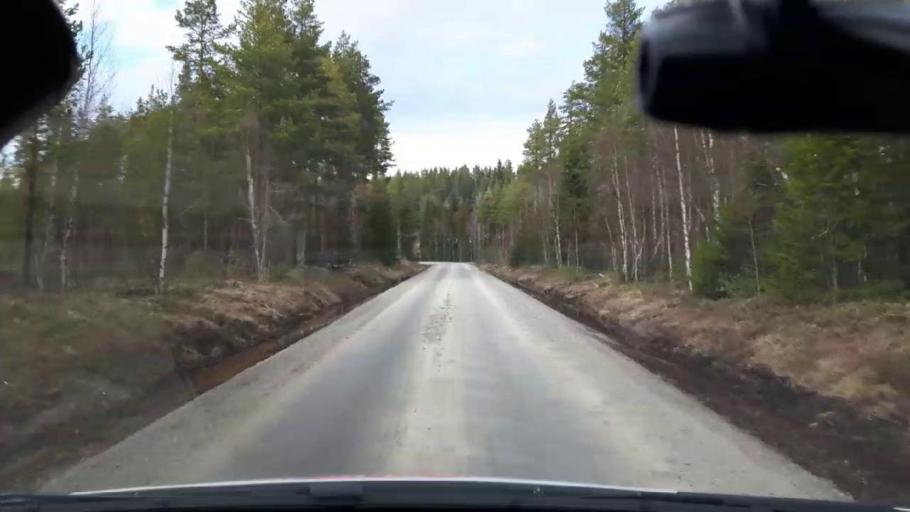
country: SE
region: Jaemtland
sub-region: OEstersunds Kommun
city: Brunflo
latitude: 62.9433
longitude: 14.6665
